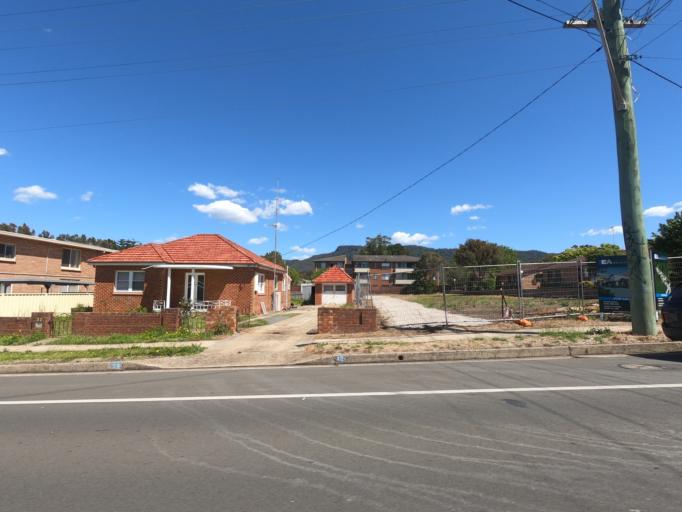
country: AU
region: New South Wales
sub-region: Wollongong
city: East Corrimal
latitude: -34.3708
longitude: 150.9099
